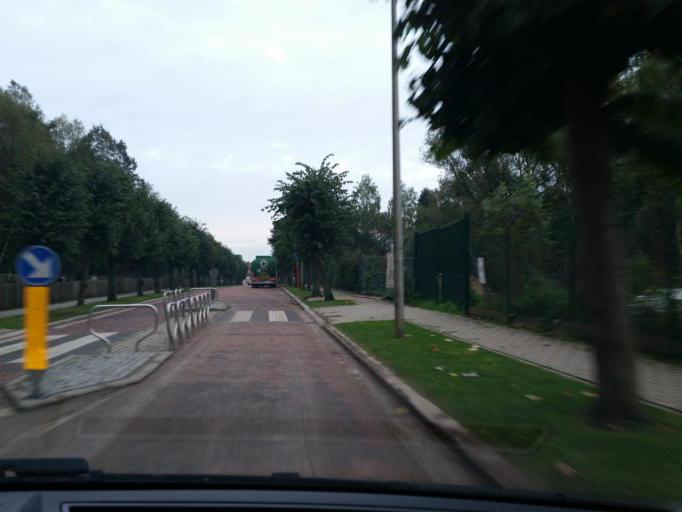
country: BE
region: Flanders
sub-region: Provincie Antwerpen
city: Hemiksem
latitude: 51.1416
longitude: 4.3339
